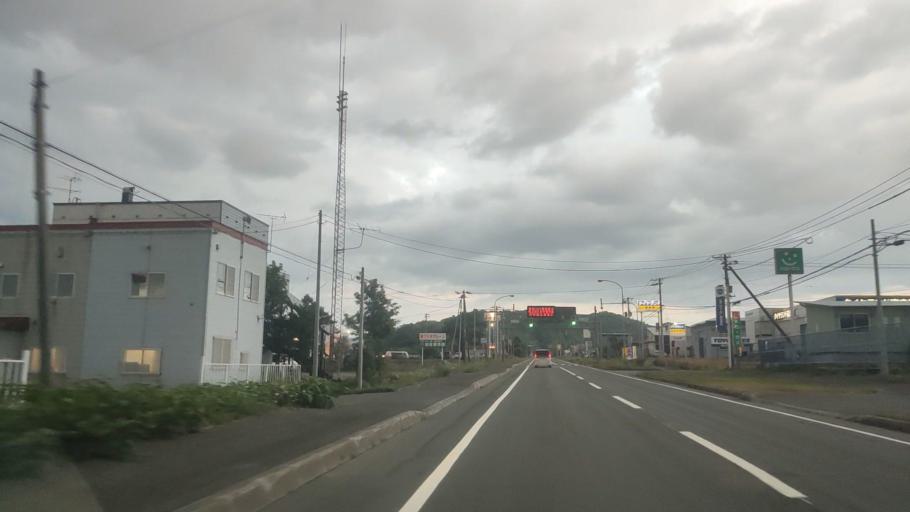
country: JP
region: Hokkaido
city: Shimo-furano
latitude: 43.3499
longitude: 142.3672
